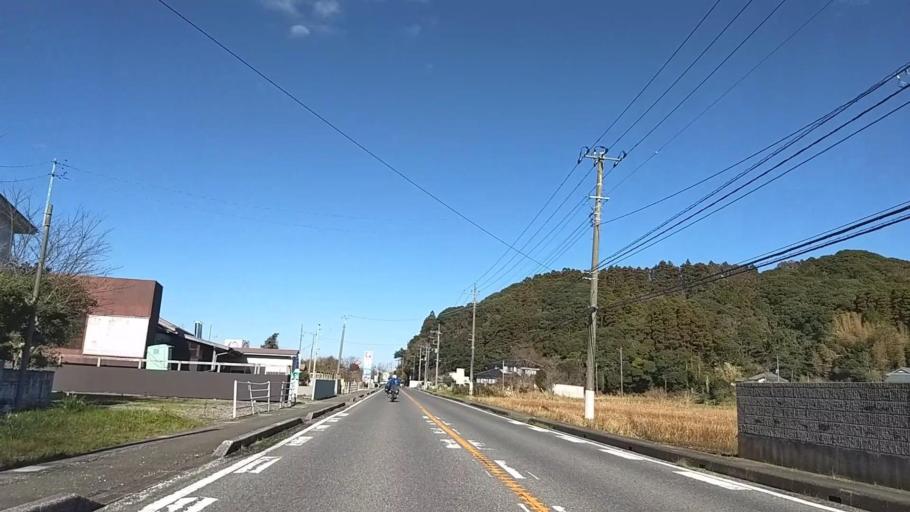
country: JP
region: Chiba
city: Ohara
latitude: 35.2246
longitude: 140.3860
